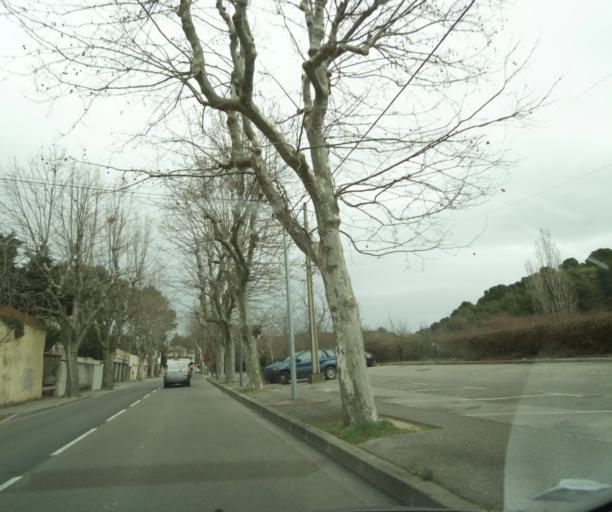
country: FR
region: Provence-Alpes-Cote d'Azur
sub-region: Departement des Bouches-du-Rhone
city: Aix-en-Provence
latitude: 43.5372
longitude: 5.4573
